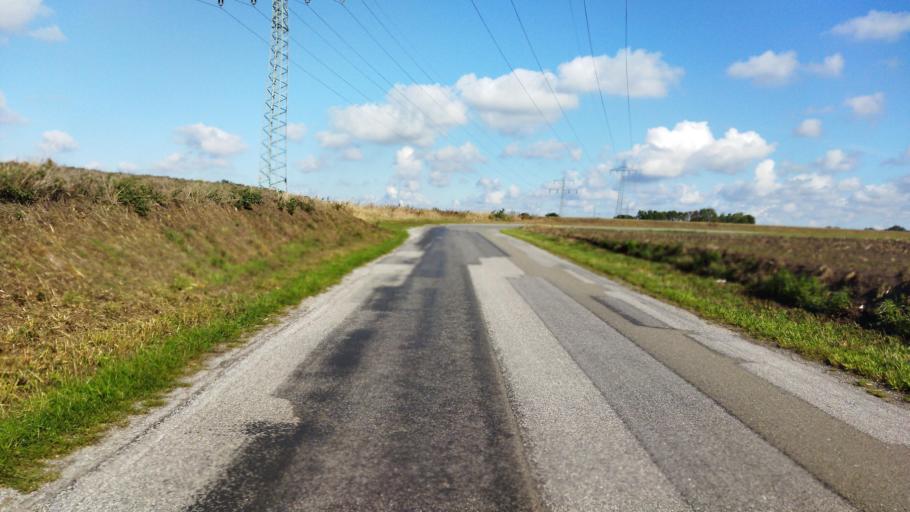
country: DE
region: Lower Saxony
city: Salzbergen
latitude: 52.3033
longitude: 7.3207
